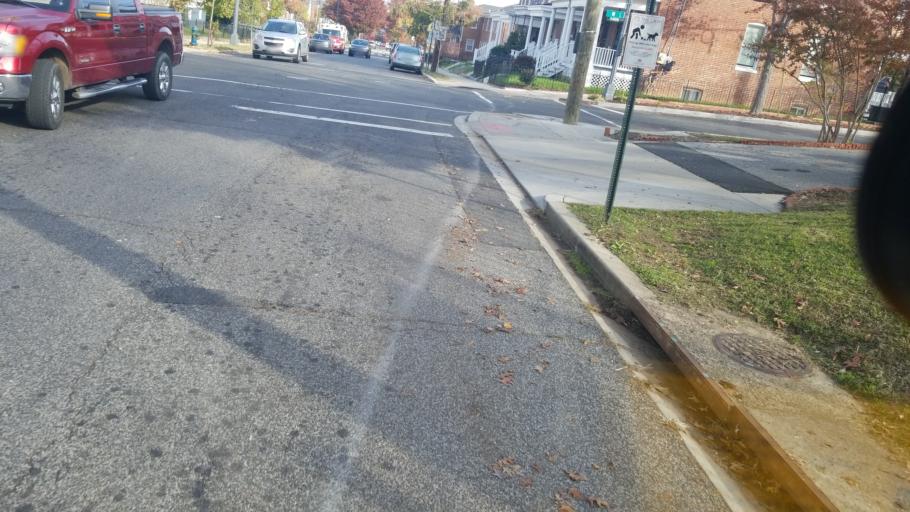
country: US
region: Maryland
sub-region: Prince George's County
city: Hillcrest Heights
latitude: 38.8640
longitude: -76.9859
